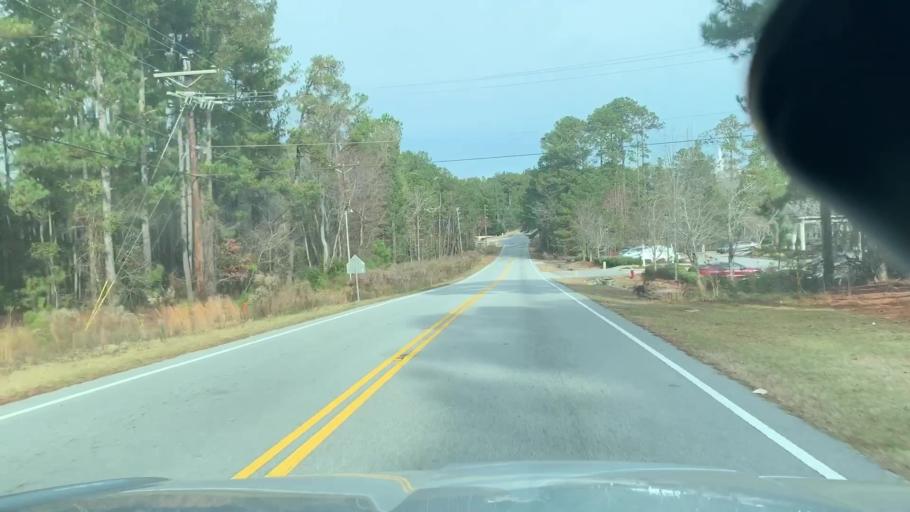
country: US
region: South Carolina
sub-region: Richland County
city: Woodfield
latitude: 34.0919
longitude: -80.8922
